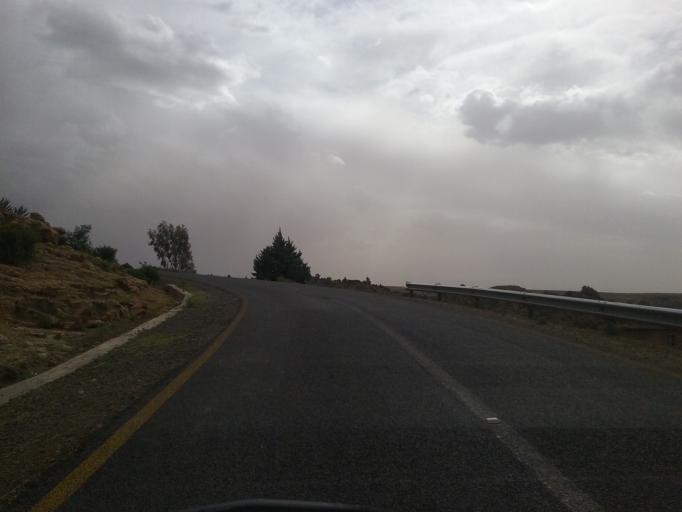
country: LS
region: Quthing
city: Quthing
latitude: -30.3710
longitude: 27.7062
